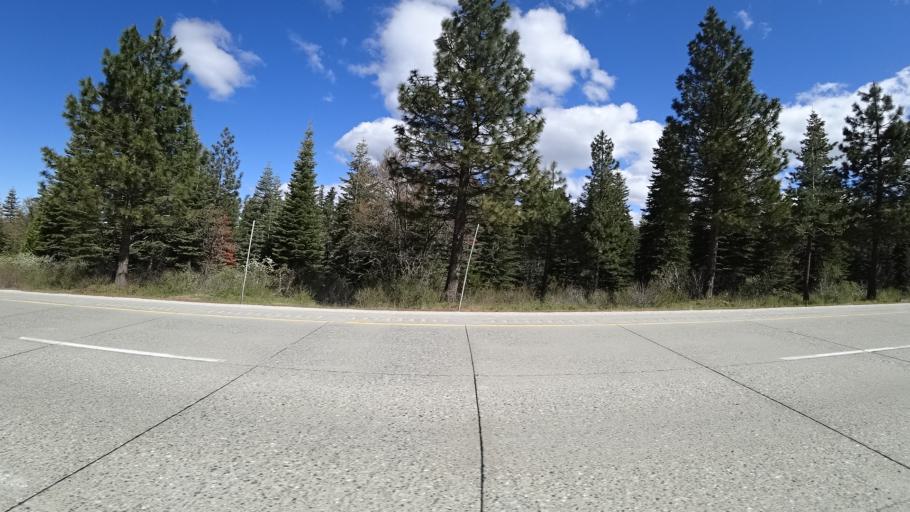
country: US
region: California
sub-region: Placer County
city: Foresthill
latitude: 39.2697
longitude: -120.7181
